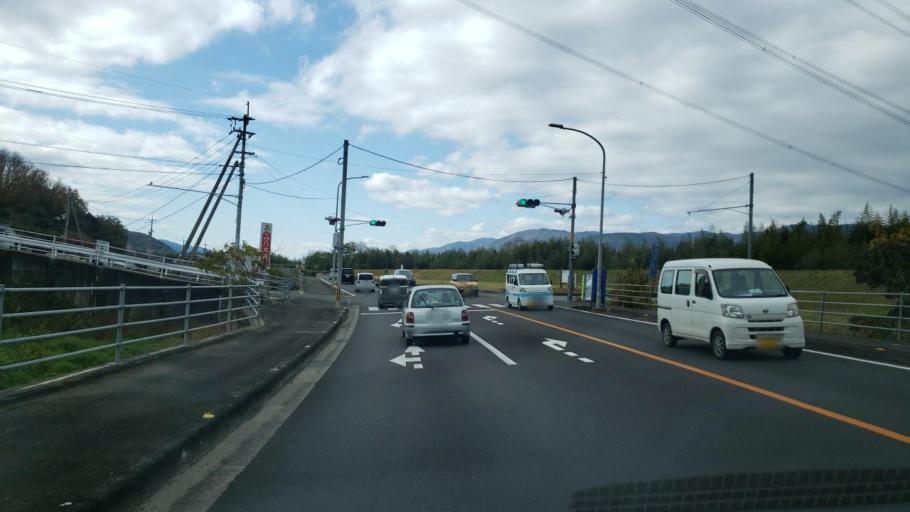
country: JP
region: Tokushima
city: Wakimachi
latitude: 34.0567
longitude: 134.1258
